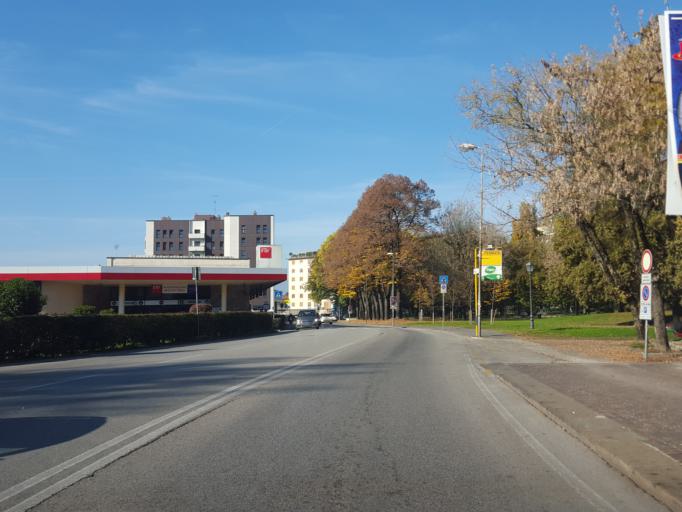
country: IT
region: Veneto
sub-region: Provincia di Vicenza
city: Vicenza
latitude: 45.5420
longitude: 11.5402
